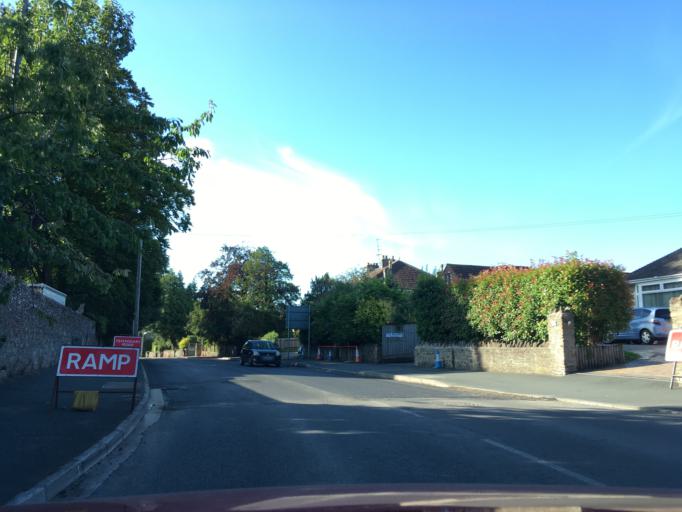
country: GB
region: England
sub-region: South Gloucestershire
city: Kingswood
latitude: 51.4406
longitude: -2.4974
